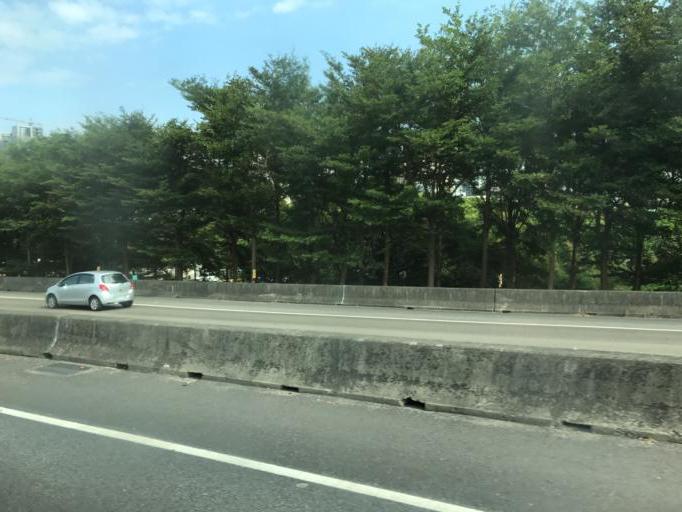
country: TW
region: Taiwan
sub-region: Hsinchu
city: Hsinchu
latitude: 24.7895
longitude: 121.0054
